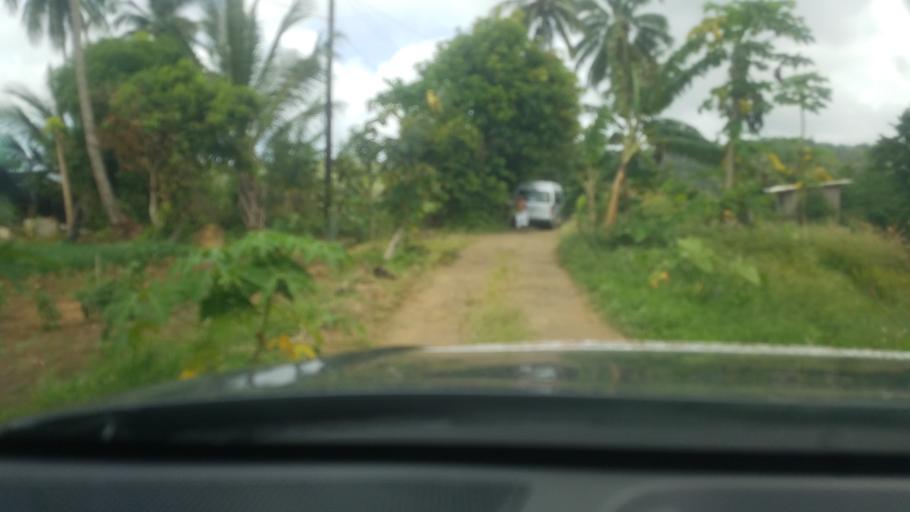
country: LC
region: Micoud Quarter
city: Micoud
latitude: 13.8040
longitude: -60.9501
